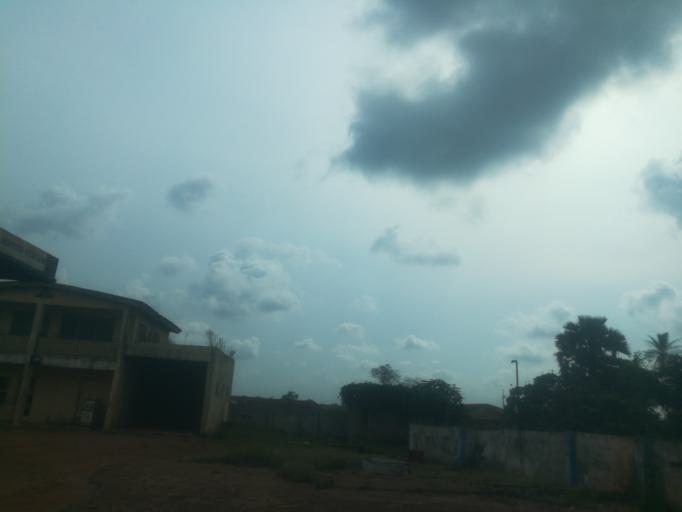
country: NG
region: Ogun
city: Ayetoro
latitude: 7.3909
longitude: 3.0161
